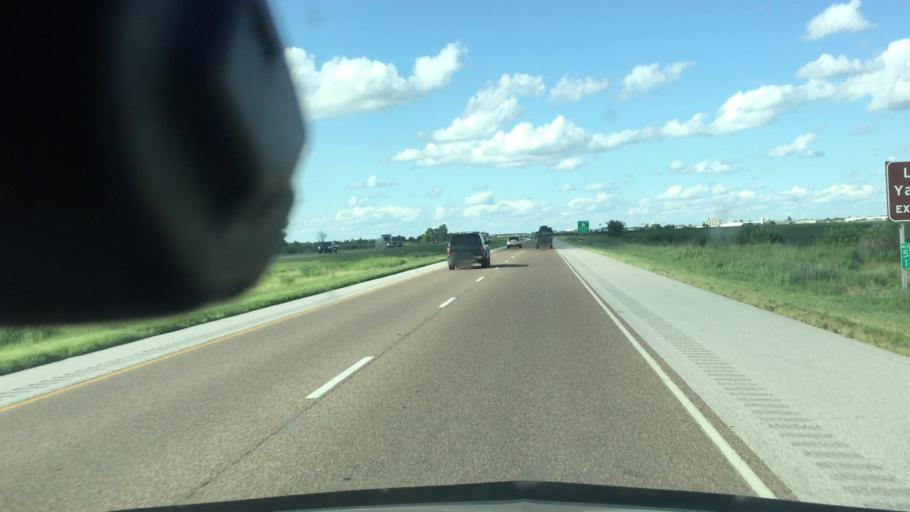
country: US
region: Illinois
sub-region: Montgomery County
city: Litchfield
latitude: 39.1556
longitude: -89.6939
